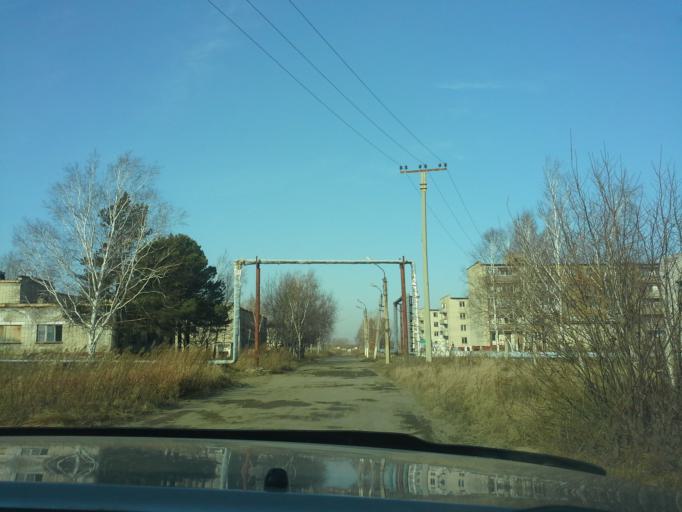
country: RU
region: Jewish Autonomous Oblast
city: Priamurskiy
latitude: 48.3586
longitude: 134.7969
